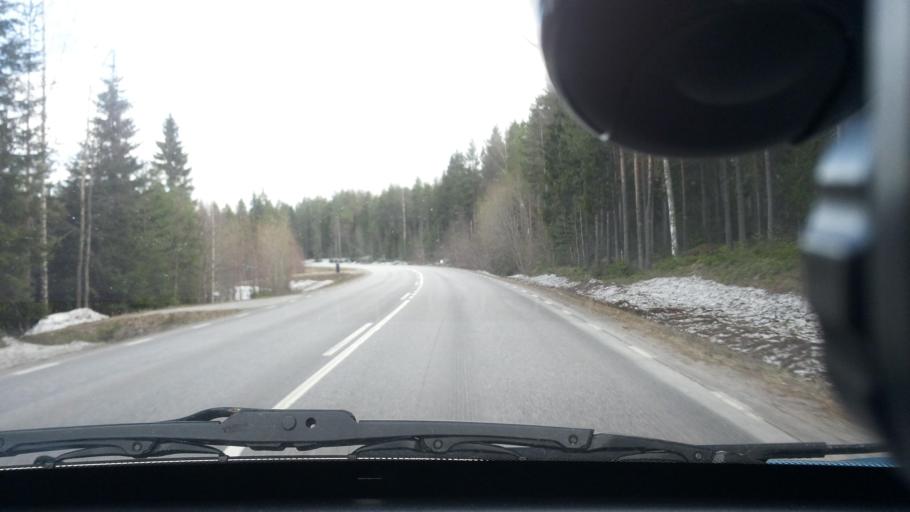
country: SE
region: Norrbotten
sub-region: Lulea Kommun
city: Gammelstad
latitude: 65.5921
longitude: 22.0005
